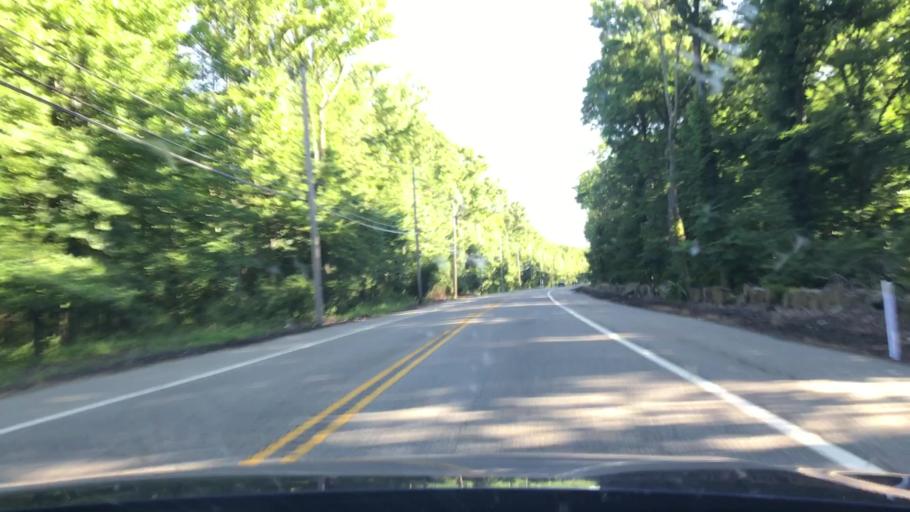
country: US
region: New Jersey
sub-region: Bergen County
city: Alpine
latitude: 40.9622
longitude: -73.9202
